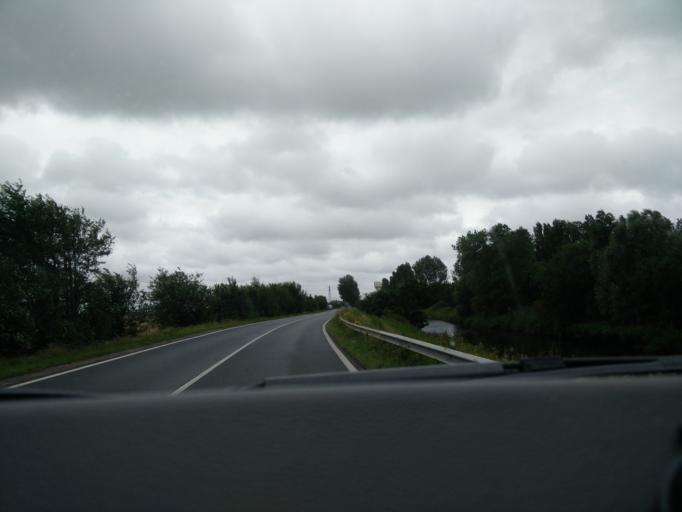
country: FR
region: Nord-Pas-de-Calais
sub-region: Departement du Nord
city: Leffrinckoucke
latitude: 51.0519
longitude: 2.4742
